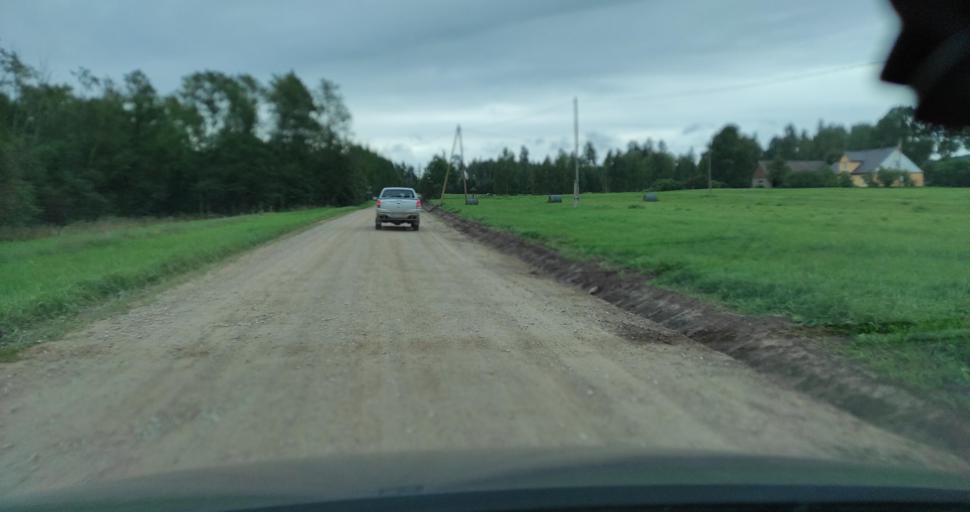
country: LV
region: Talsu Rajons
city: Stende
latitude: 57.0481
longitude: 22.3027
